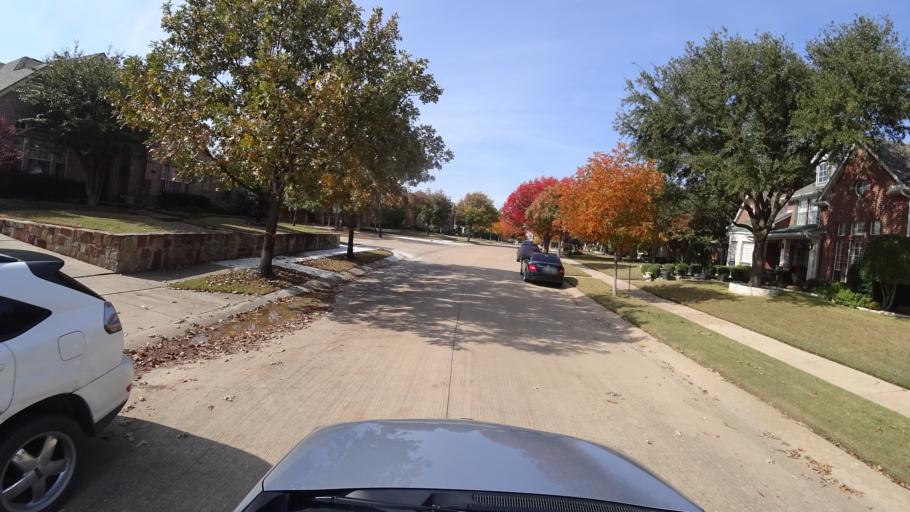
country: US
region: Texas
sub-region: Denton County
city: The Colony
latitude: 33.0339
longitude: -96.8893
